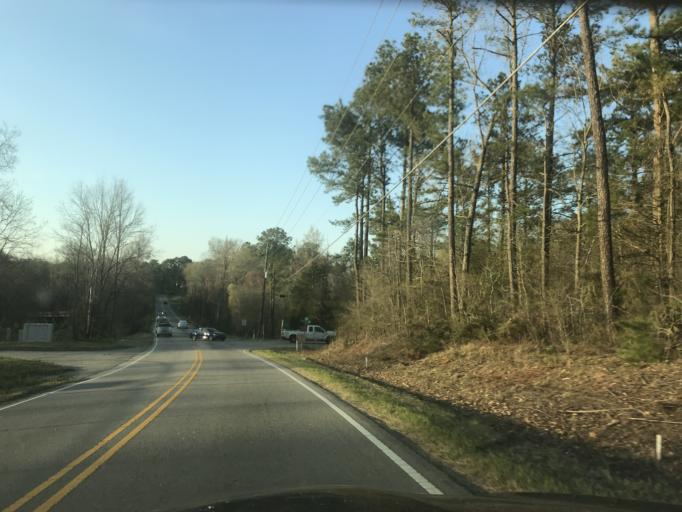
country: US
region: North Carolina
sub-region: Wake County
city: Knightdale
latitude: 35.7482
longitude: -78.5343
